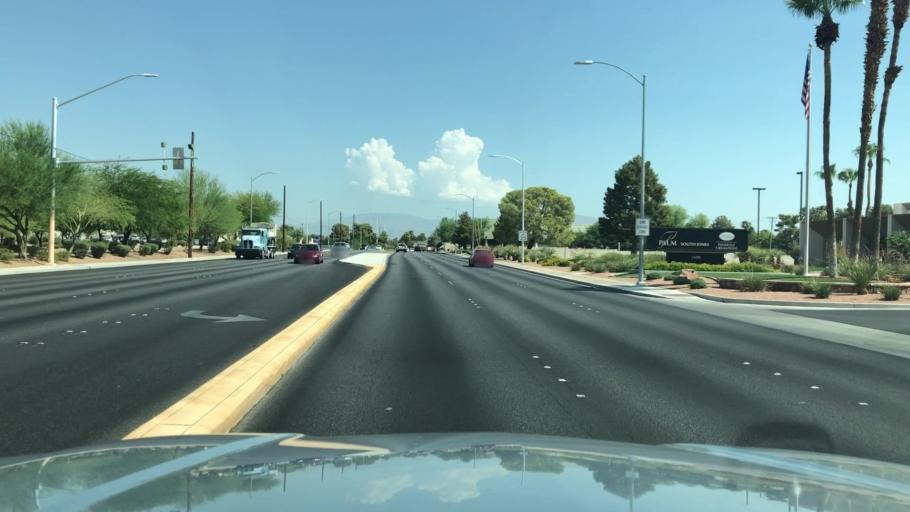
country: US
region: Nevada
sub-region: Clark County
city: Spring Valley
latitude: 36.1524
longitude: -115.2256
